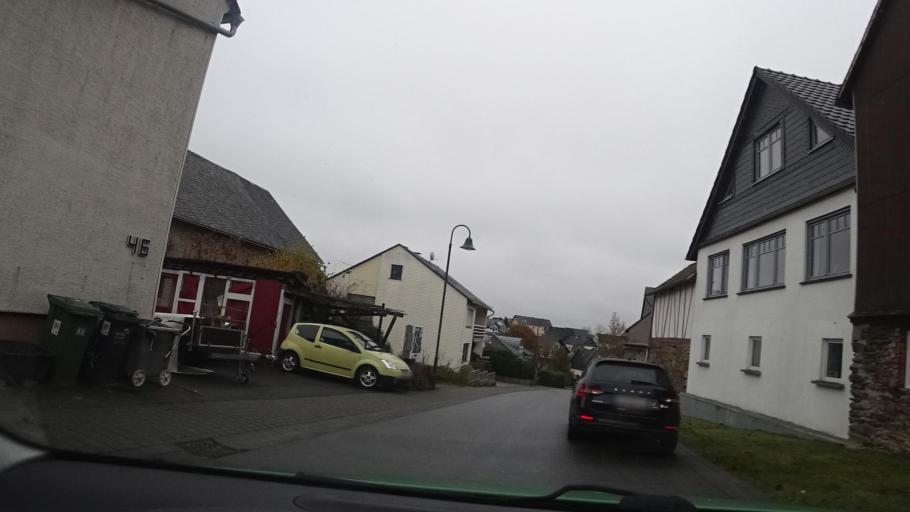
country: DE
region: Rheinland-Pfalz
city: Maisborn
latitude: 50.0788
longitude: 7.6016
